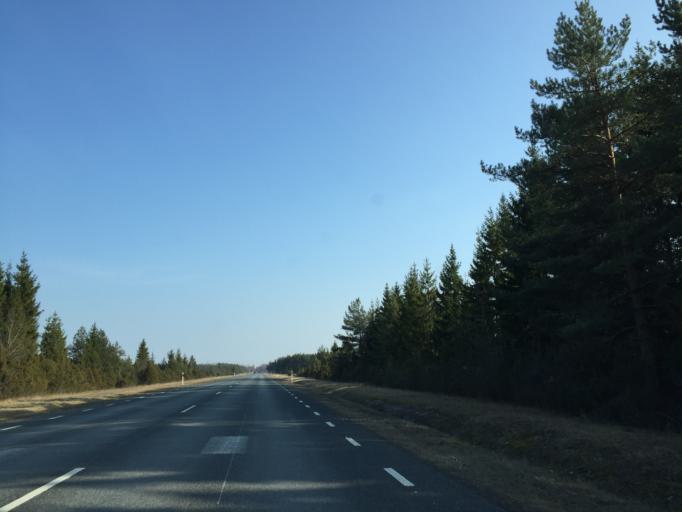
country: EE
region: Saare
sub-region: Orissaare vald
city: Orissaare
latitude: 58.5906
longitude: 23.3358
